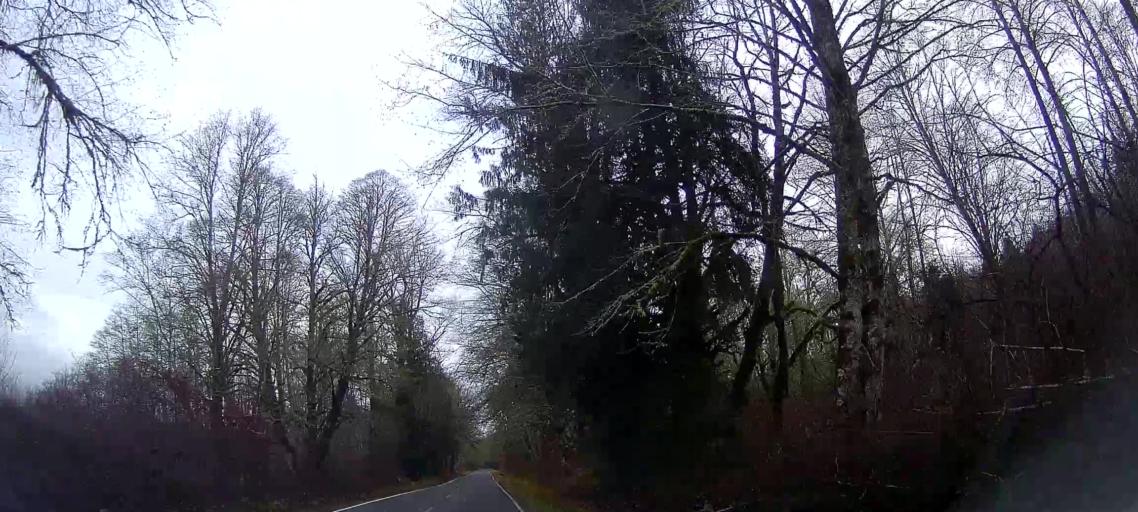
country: US
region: Washington
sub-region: Skagit County
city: Sedro-Woolley
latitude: 48.5142
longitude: -121.8757
